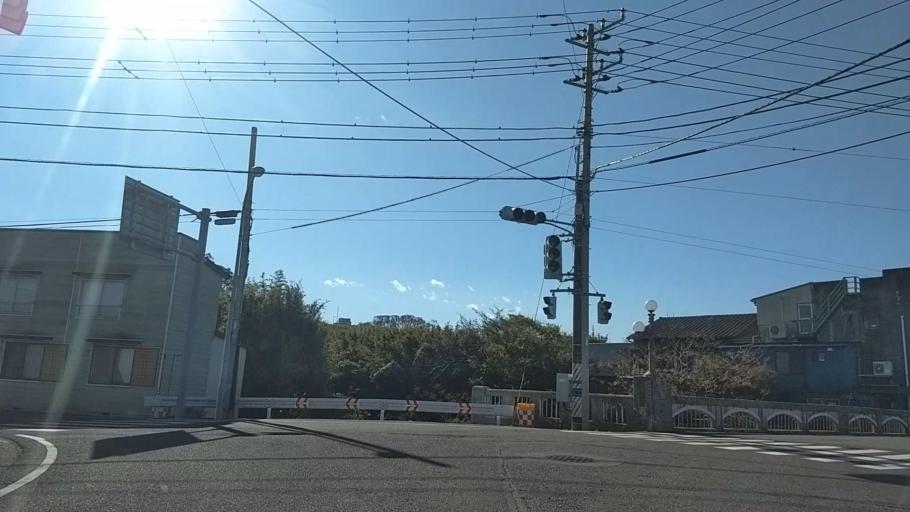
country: JP
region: Chiba
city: Tateyama
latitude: 34.9860
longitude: 139.8623
